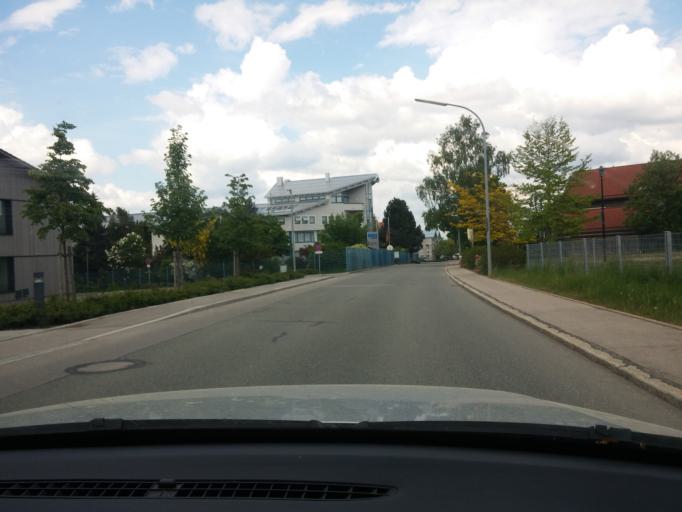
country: DE
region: Bavaria
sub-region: Upper Bavaria
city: Holzkirchen
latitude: 47.8815
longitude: 11.7090
